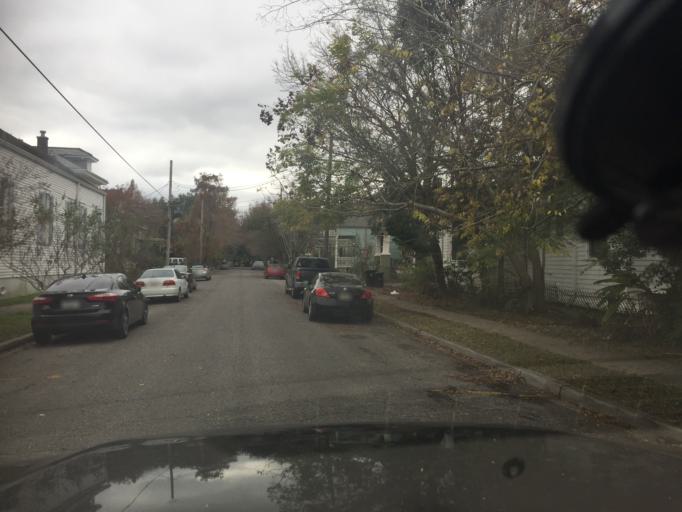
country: US
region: Louisiana
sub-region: Orleans Parish
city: New Orleans
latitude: 29.9768
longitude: -90.0821
